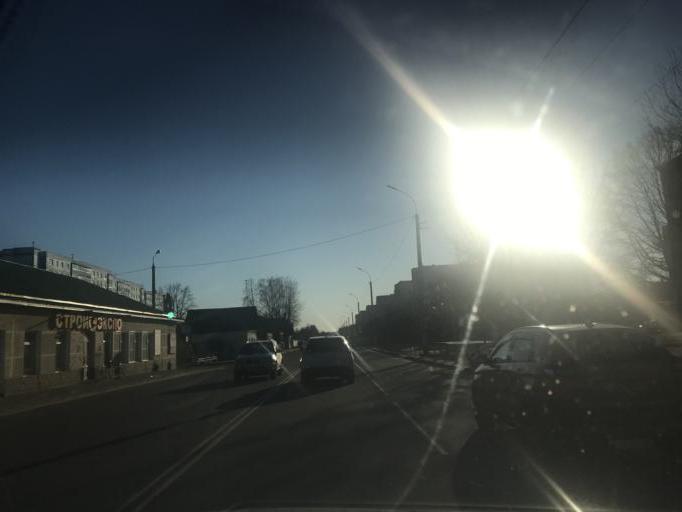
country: BY
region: Mogilev
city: Mahilyow
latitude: 53.8775
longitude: 30.3367
